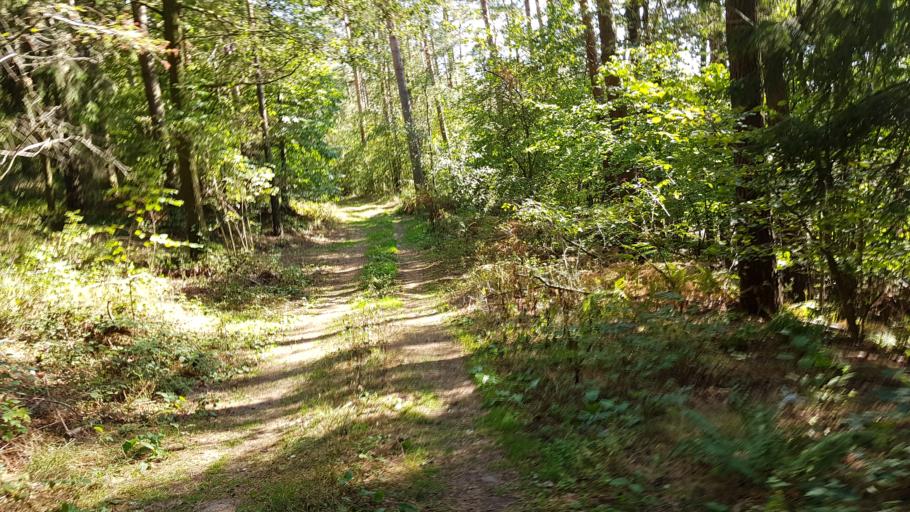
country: DE
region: Saxony
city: Grossnaundorf
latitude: 51.2187
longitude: 13.9501
